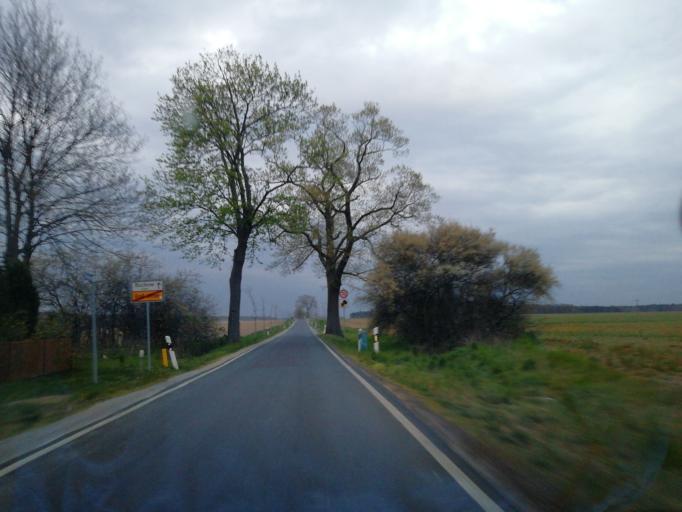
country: DE
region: Brandenburg
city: Calau
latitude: 51.7724
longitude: 13.8813
